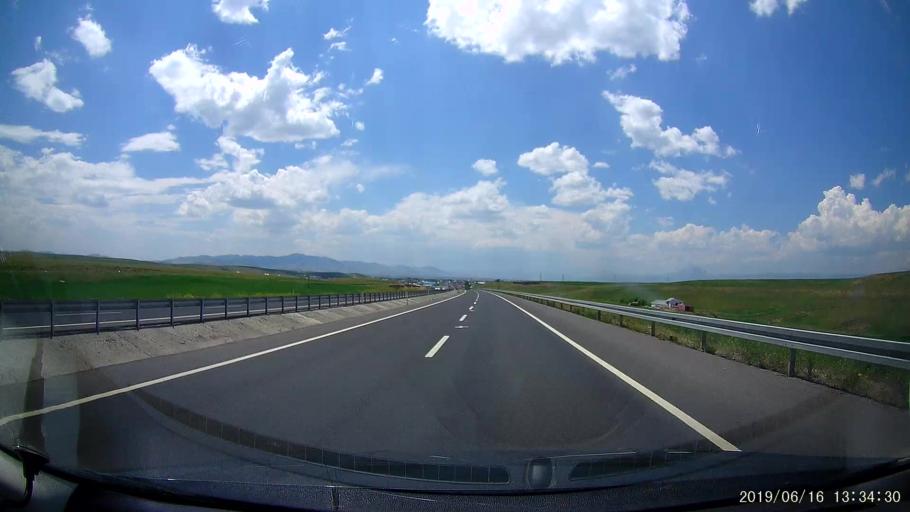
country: TR
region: Agri
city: Agri
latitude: 39.7129
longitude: 43.1245
